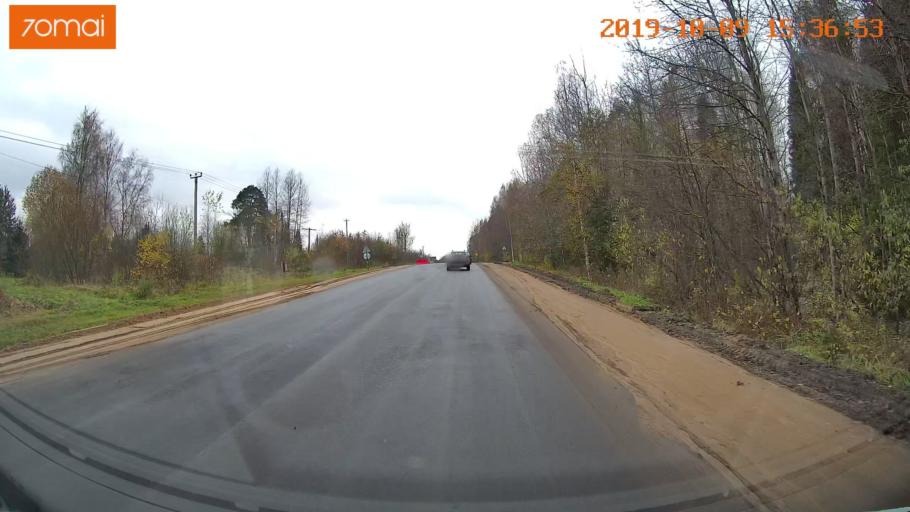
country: RU
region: Kostroma
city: Oktyabr'skiy
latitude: 57.9218
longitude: 41.2066
